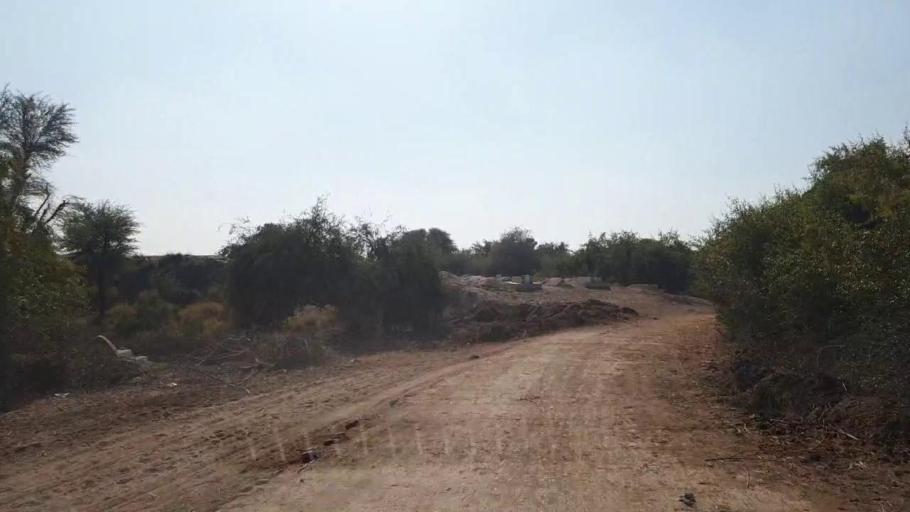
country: PK
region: Sindh
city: Bhit Shah
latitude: 25.9249
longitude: 68.4850
